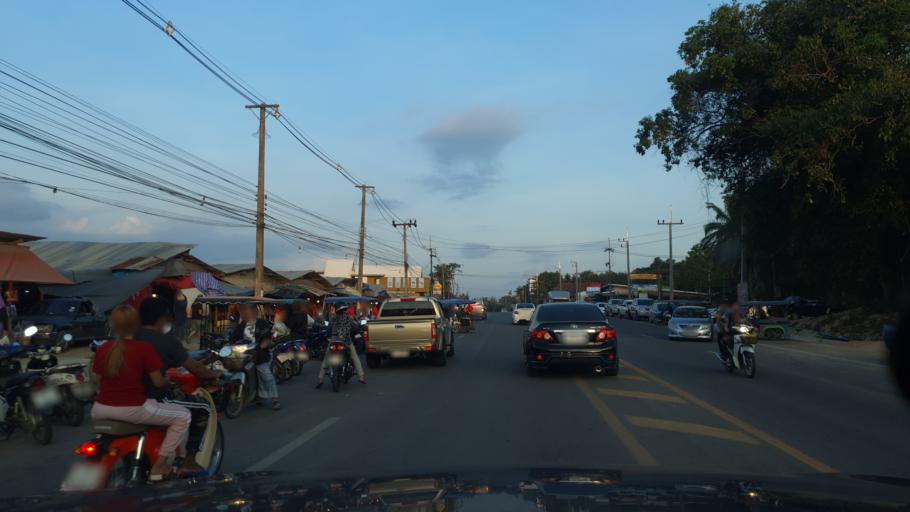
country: TH
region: Phangnga
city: Ban Ao Nang
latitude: 8.0419
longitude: 98.8428
